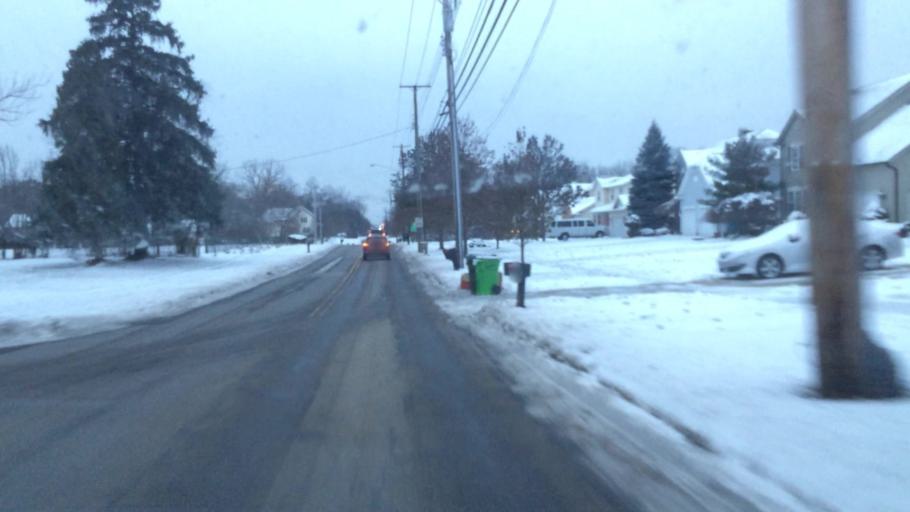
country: US
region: Ohio
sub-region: Cuyahoga County
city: Oakwood
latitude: 41.3727
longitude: -81.5017
